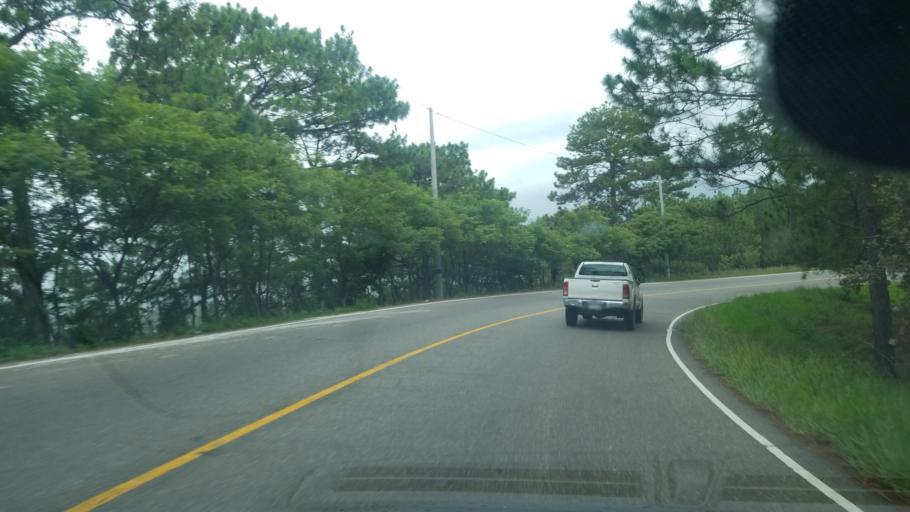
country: HN
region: Ocotepeque
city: Sinuapa
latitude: 14.4600
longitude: -89.1598
